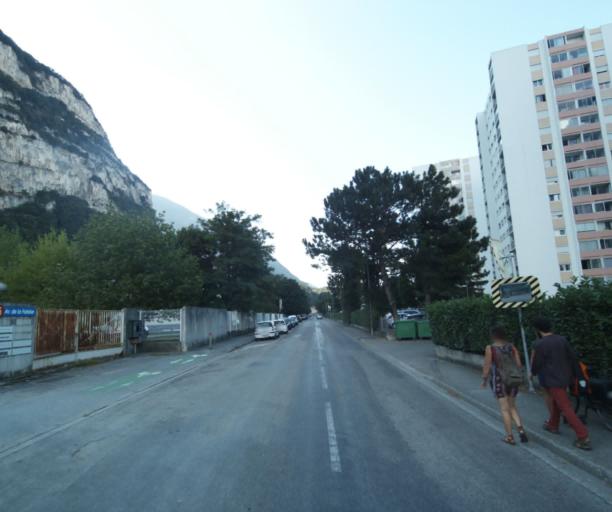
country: FR
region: Rhone-Alpes
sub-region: Departement de l'Isere
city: Sassenage
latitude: 45.2024
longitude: 5.6633
